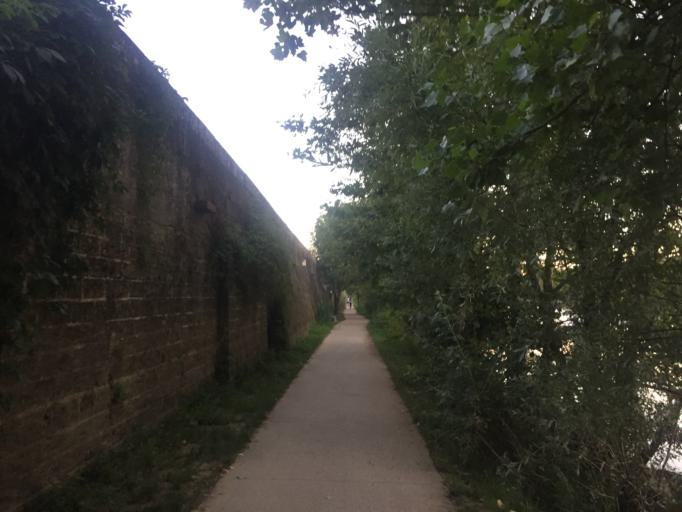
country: FR
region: Rhone-Alpes
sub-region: Departement du Rhone
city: Caluire-et-Cuire
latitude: 45.7887
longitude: 4.8191
